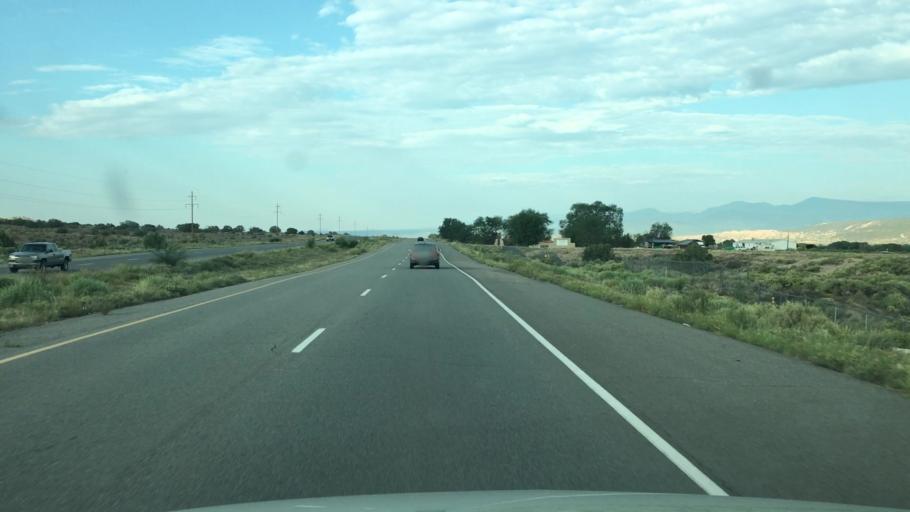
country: US
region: New Mexico
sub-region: Rio Arriba County
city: Ohkay Owingeh
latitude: 36.1312
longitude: -106.0015
